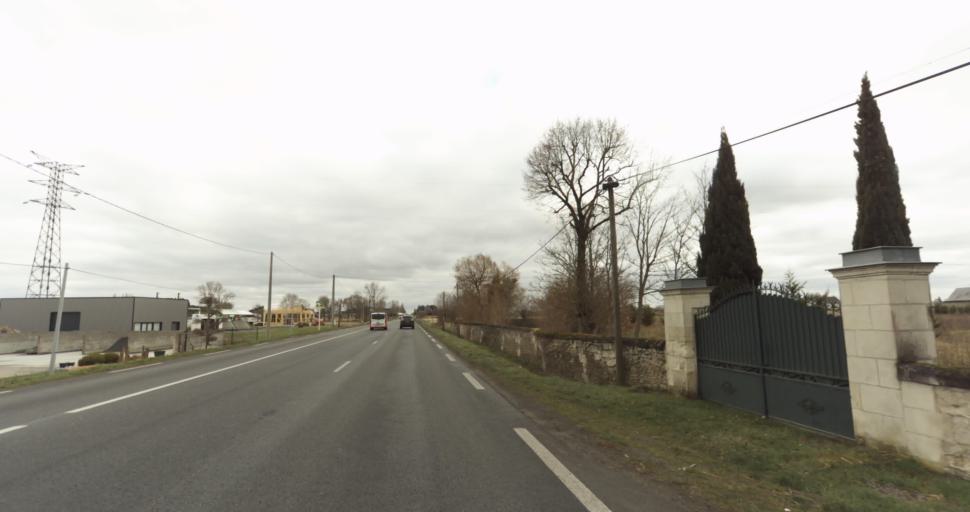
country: FR
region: Pays de la Loire
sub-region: Departement de Maine-et-Loire
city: Vivy
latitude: 47.3663
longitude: -0.0947
